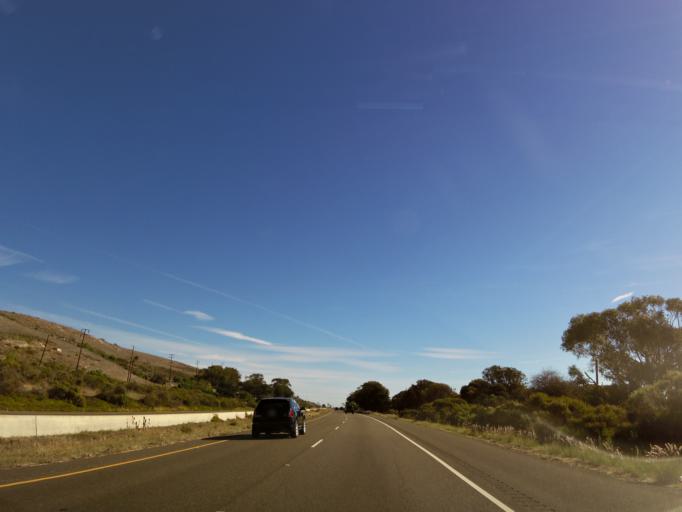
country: US
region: California
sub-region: Santa Barbara County
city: Solvang
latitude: 34.4682
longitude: -120.1104
